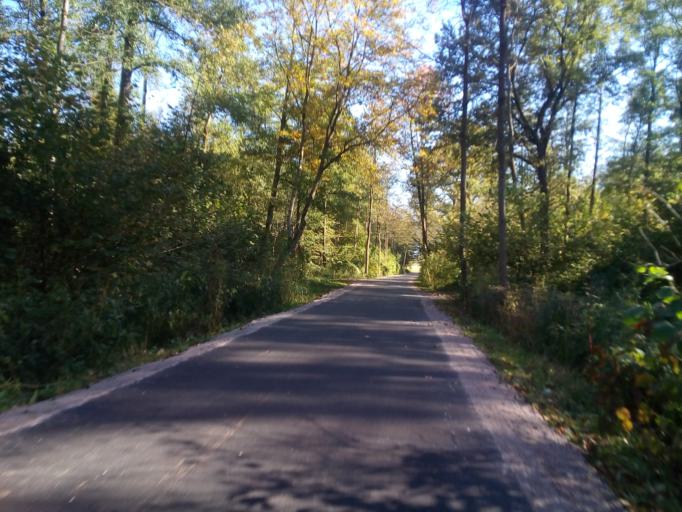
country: DE
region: Baden-Wuerttemberg
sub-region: Karlsruhe Region
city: Zell
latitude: 48.6876
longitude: 8.0436
